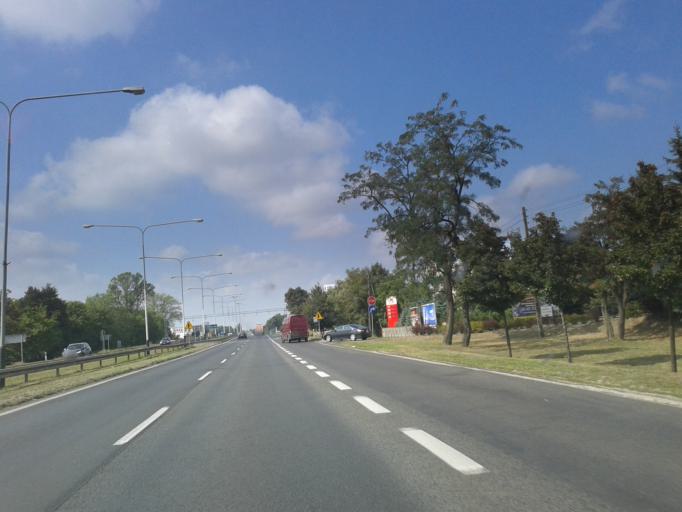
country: PL
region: Greater Poland Voivodeship
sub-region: Powiat poznanski
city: Baranowo
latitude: 52.4332
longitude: 16.8013
